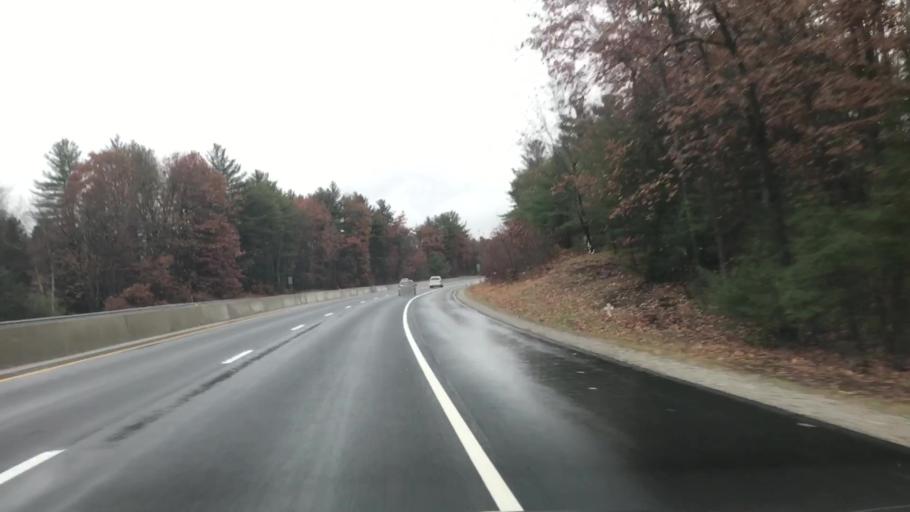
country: US
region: New Hampshire
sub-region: Hillsborough County
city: Pinardville
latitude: 43.0345
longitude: -71.4855
